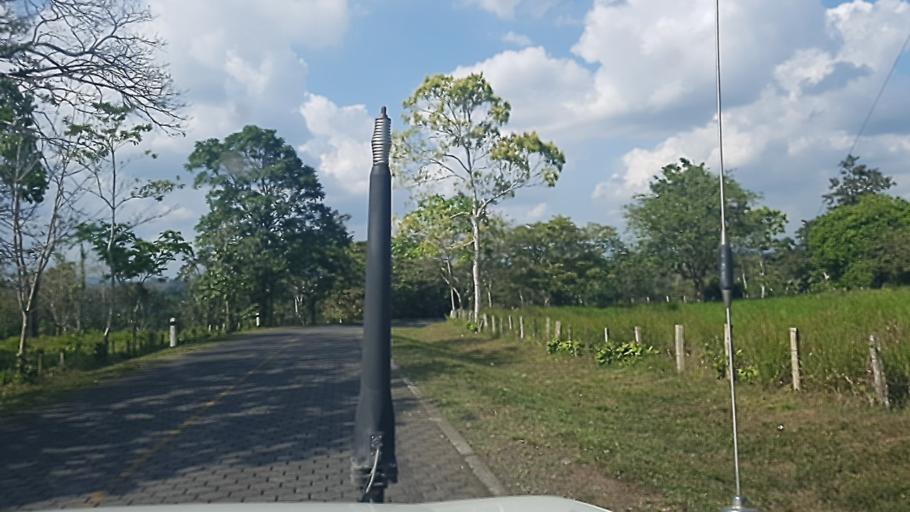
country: NI
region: Atlantico Sur
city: Nueva Guinea
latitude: 11.6980
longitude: -84.3964
